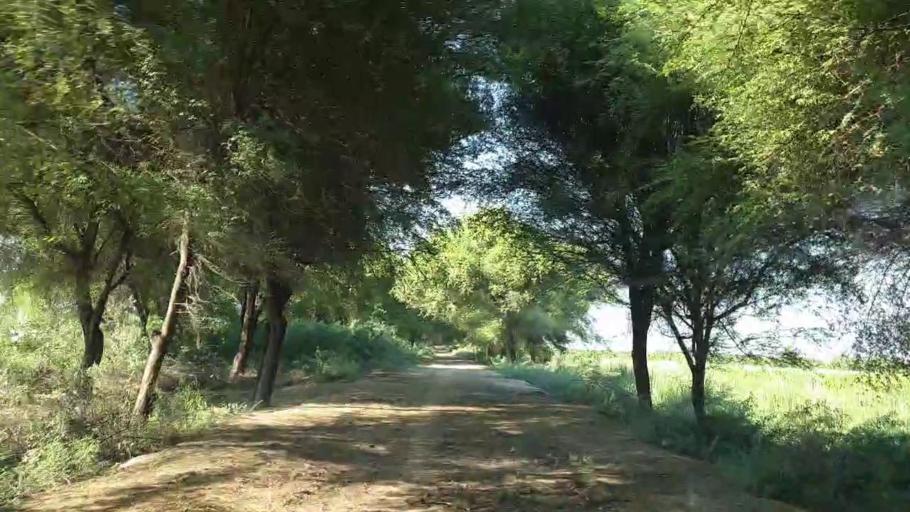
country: PK
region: Sindh
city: Tando Jam
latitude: 25.3557
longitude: 68.5699
